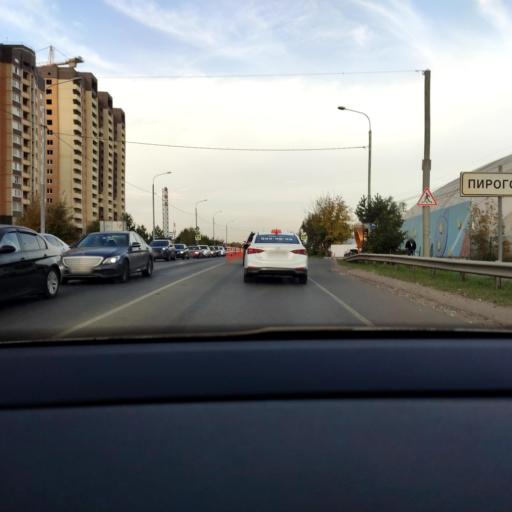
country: RU
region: Moskovskaya
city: Pirogovskiy
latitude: 55.9718
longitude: 37.7411
